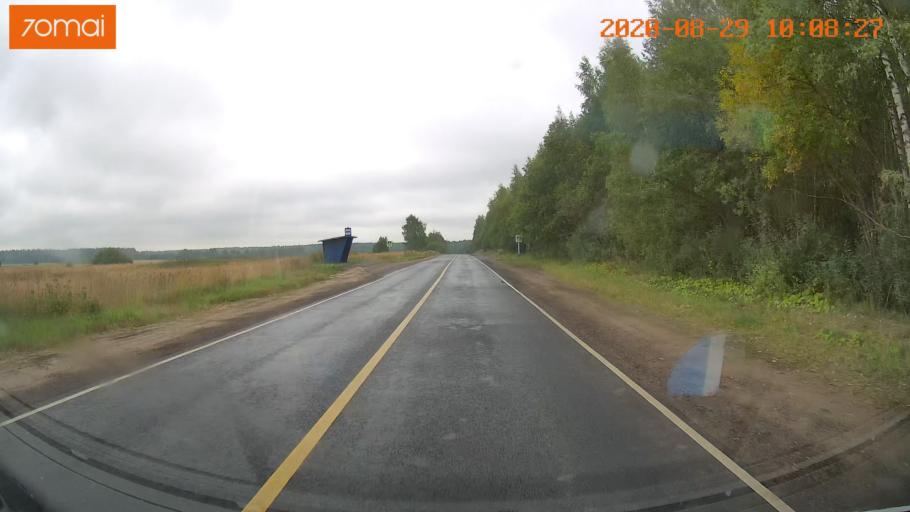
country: RU
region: Ivanovo
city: Kuznechikha
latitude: 57.3761
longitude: 42.5905
